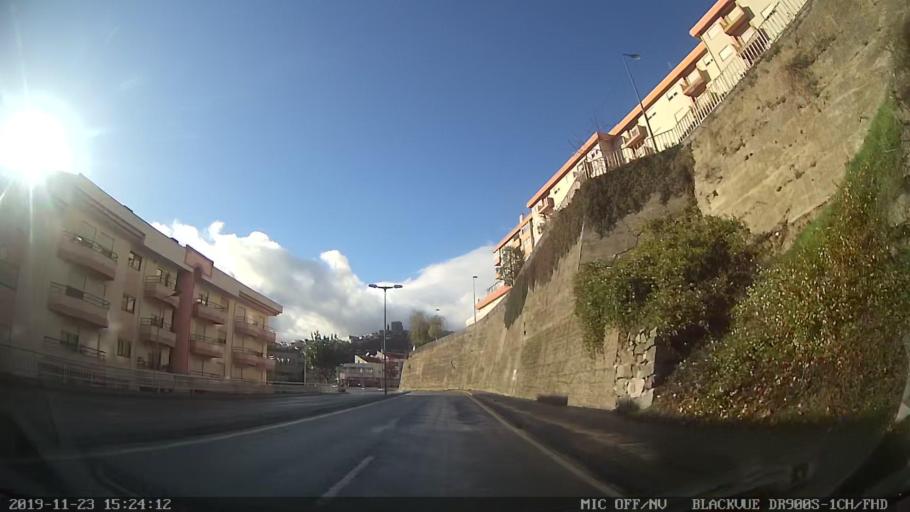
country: PT
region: Viseu
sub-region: Lamego
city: Lamego
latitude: 41.0991
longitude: -7.8028
